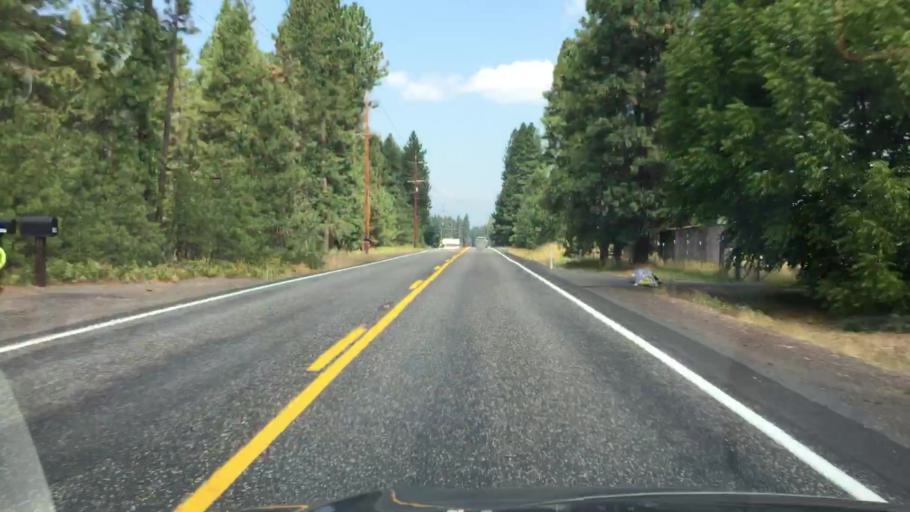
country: US
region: Washington
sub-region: Klickitat County
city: White Salmon
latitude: 45.9467
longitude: -121.4909
